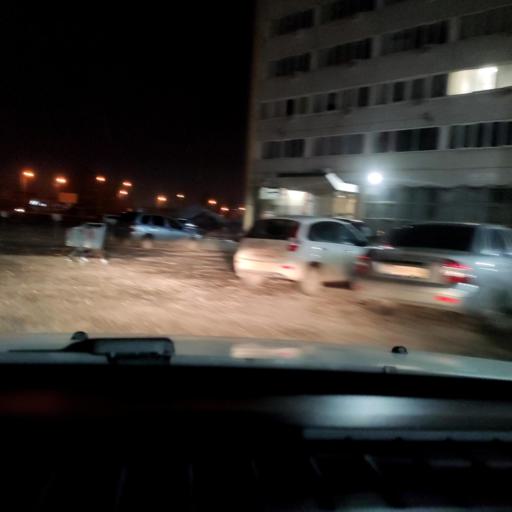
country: RU
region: Samara
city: Tol'yatti
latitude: 53.5599
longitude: 49.3133
